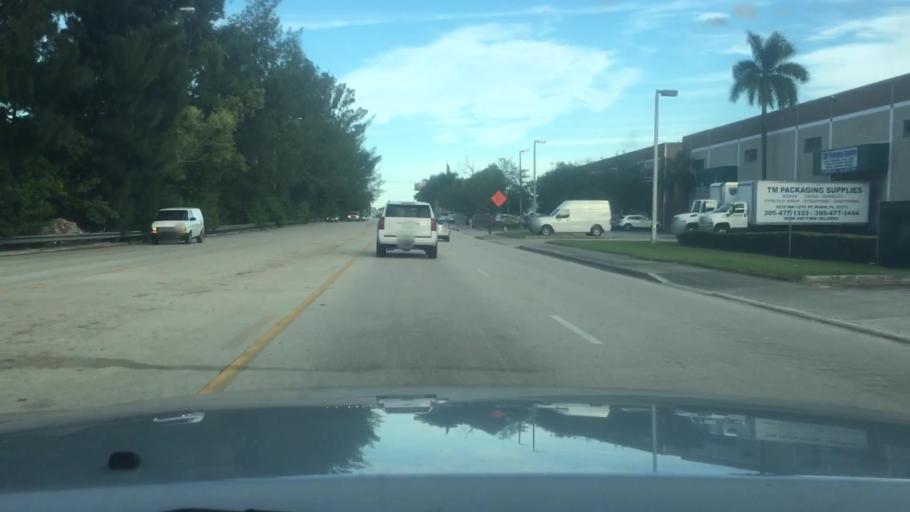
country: US
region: Florida
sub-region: Miami-Dade County
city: Fountainebleau
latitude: 25.7832
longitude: -80.3455
